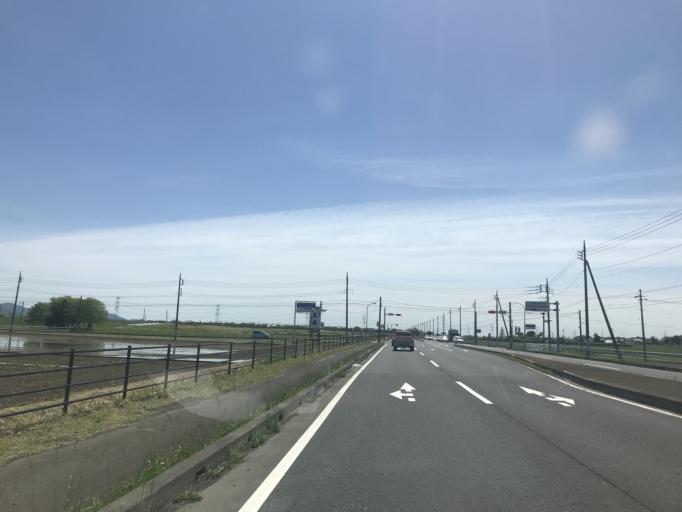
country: JP
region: Ibaraki
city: Shimodate
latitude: 36.2734
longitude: 139.9797
